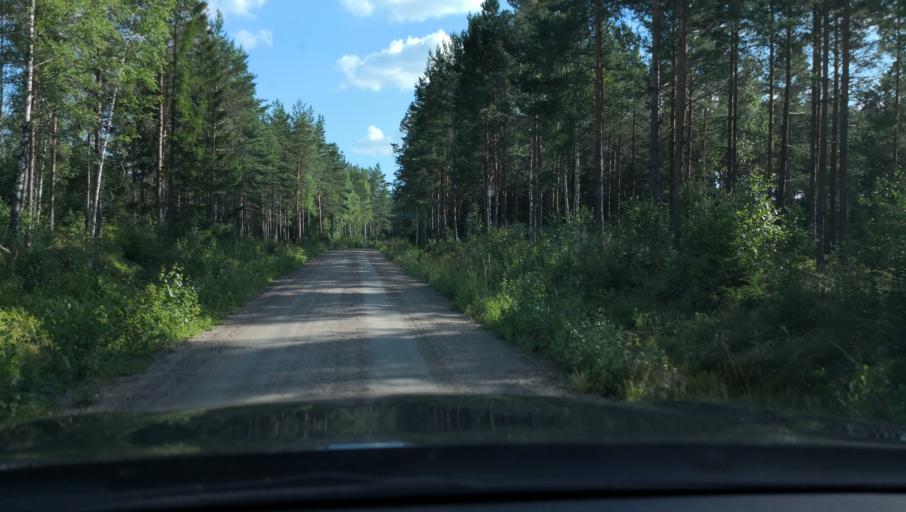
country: SE
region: Vaestmanland
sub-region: Vasteras
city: Skultuna
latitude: 59.7183
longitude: 16.3724
